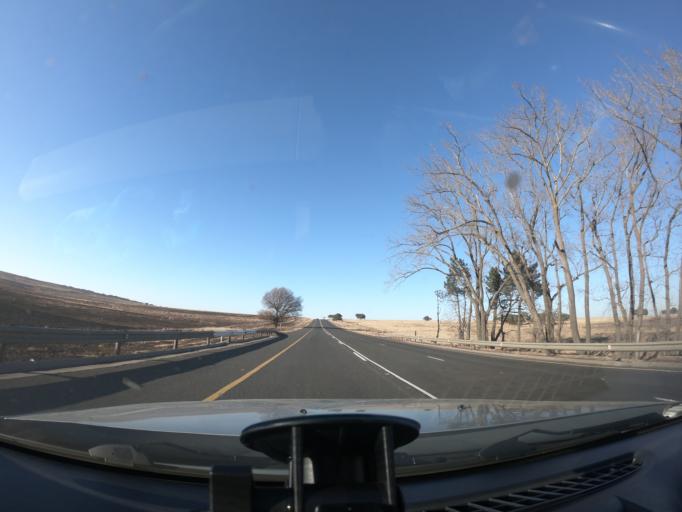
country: ZA
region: Mpumalanga
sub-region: Gert Sibande District Municipality
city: Ermelo
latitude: -26.4503
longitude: 29.9496
